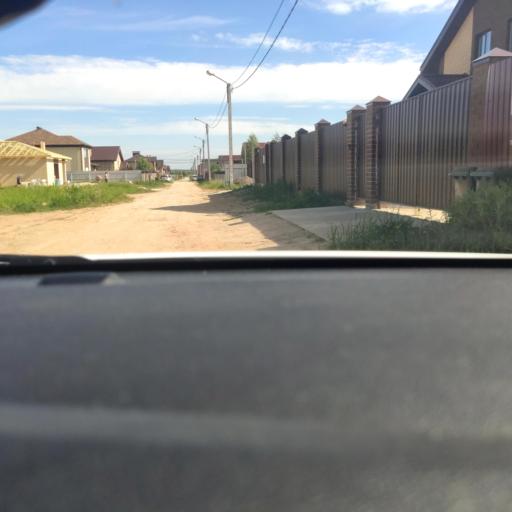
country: RU
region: Tatarstan
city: Vysokaya Gora
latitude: 55.8199
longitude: 49.3086
